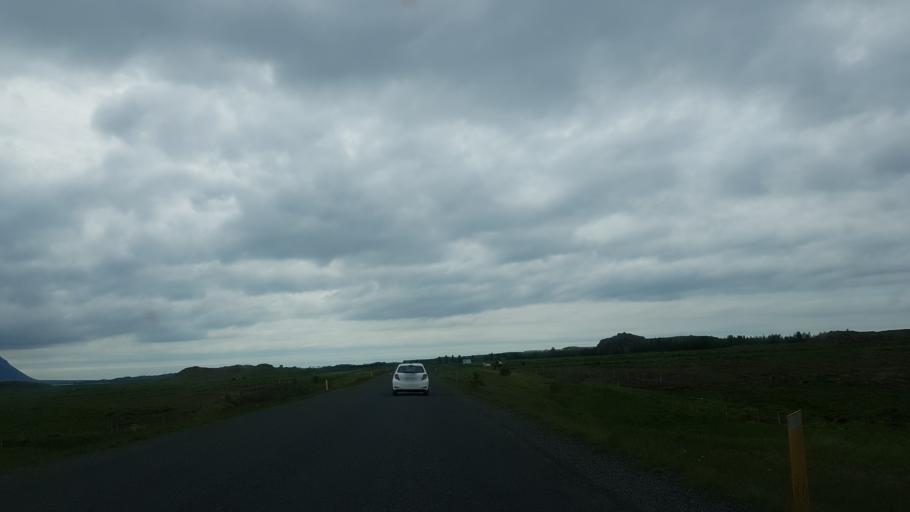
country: IS
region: West
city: Borgarnes
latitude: 64.5868
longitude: -21.8564
